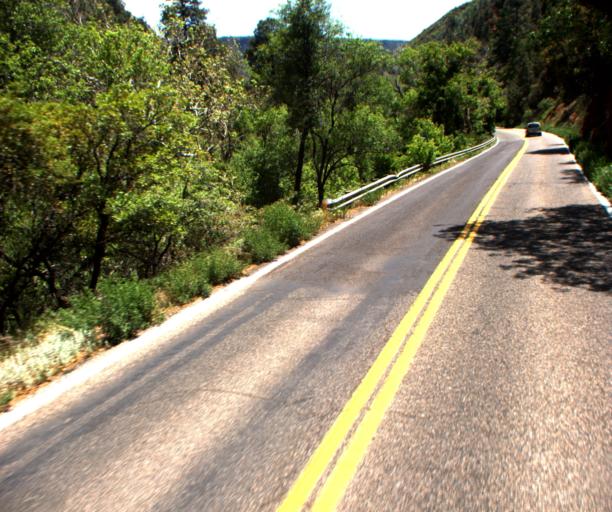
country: US
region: Arizona
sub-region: Coconino County
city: Sedona
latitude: 34.9317
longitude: -111.7413
